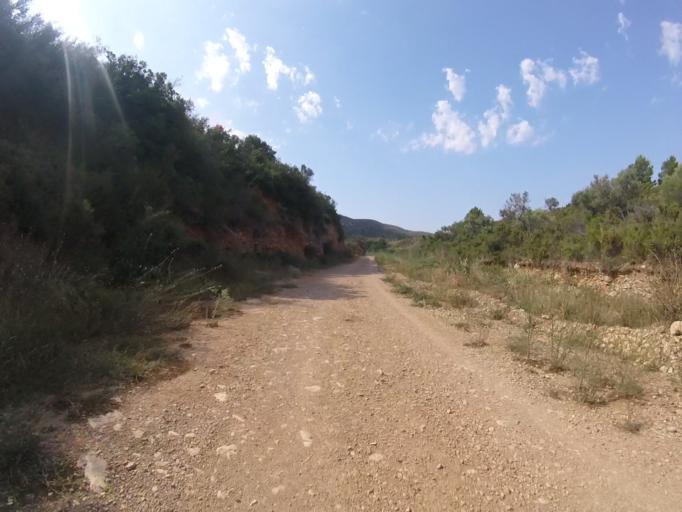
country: ES
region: Valencia
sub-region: Provincia de Castello
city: Alcala de Xivert
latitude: 40.3206
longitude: 0.1859
